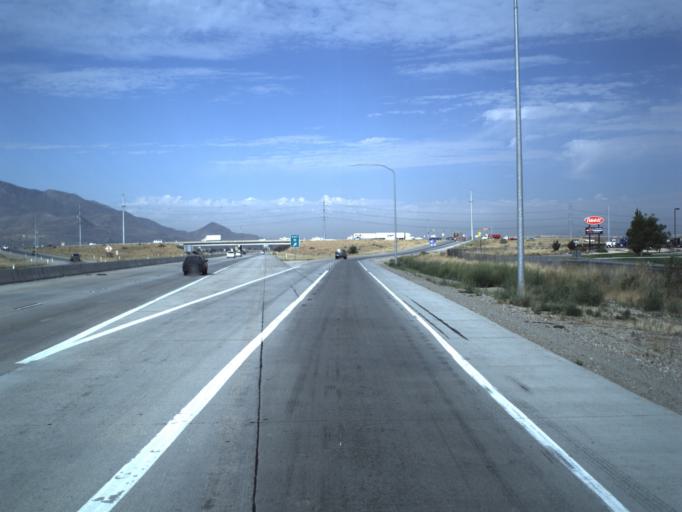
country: US
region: Utah
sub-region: Salt Lake County
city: West Valley City
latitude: 40.7259
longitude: -112.0188
